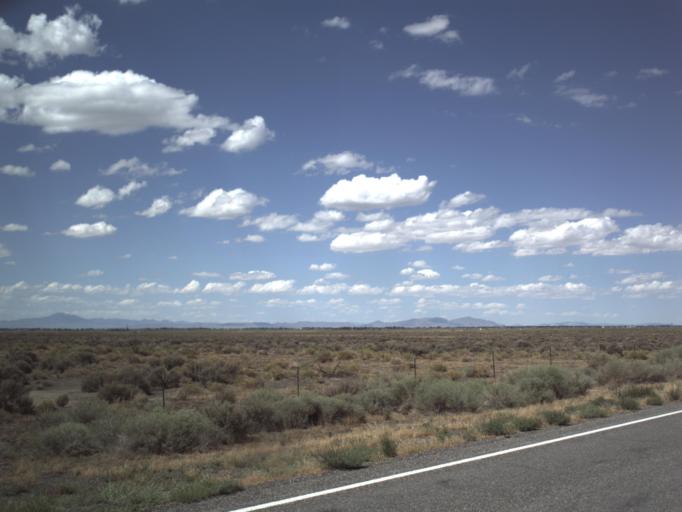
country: US
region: Utah
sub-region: Millard County
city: Delta
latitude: 39.2735
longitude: -112.4558
